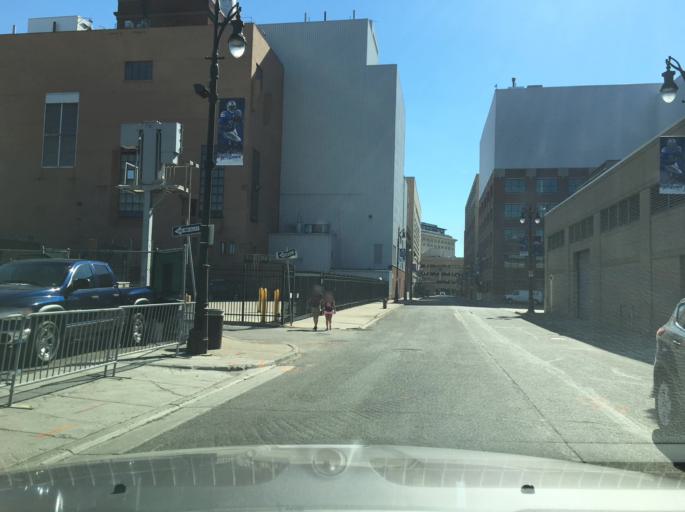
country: US
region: Michigan
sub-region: Wayne County
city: Detroit
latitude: 42.3391
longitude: -83.0435
